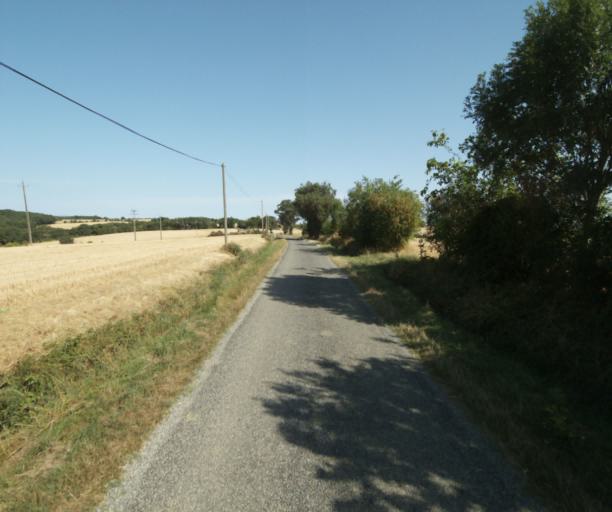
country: FR
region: Midi-Pyrenees
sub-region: Departement de la Haute-Garonne
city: Saint-Felix-Lauragais
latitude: 43.4277
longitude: 1.8272
